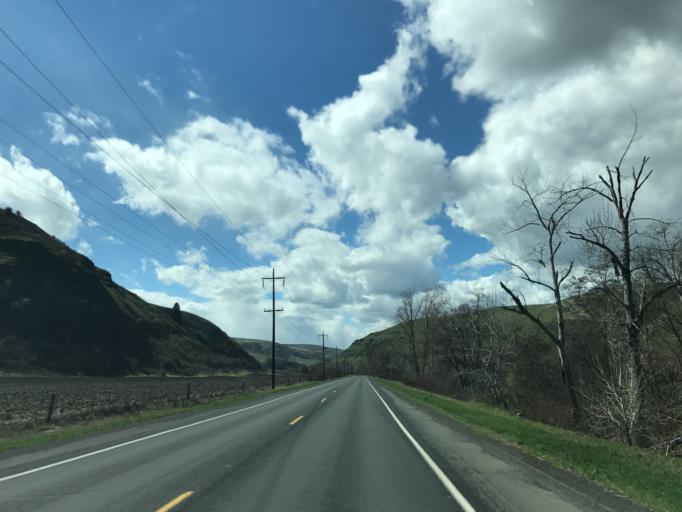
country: US
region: Idaho
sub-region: Nez Perce County
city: Lapwai
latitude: 46.3668
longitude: -116.7372
